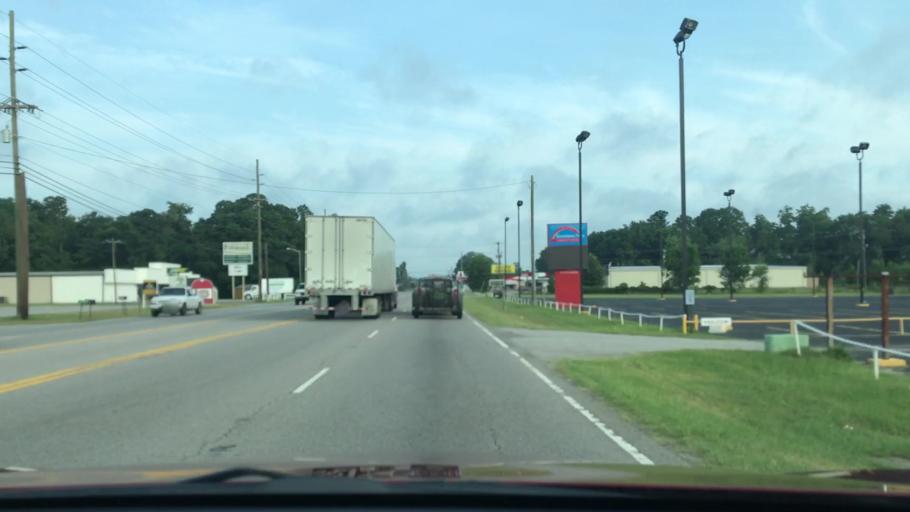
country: US
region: South Carolina
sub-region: Orangeburg County
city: Wilkinson Heights
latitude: 33.4805
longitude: -80.8223
